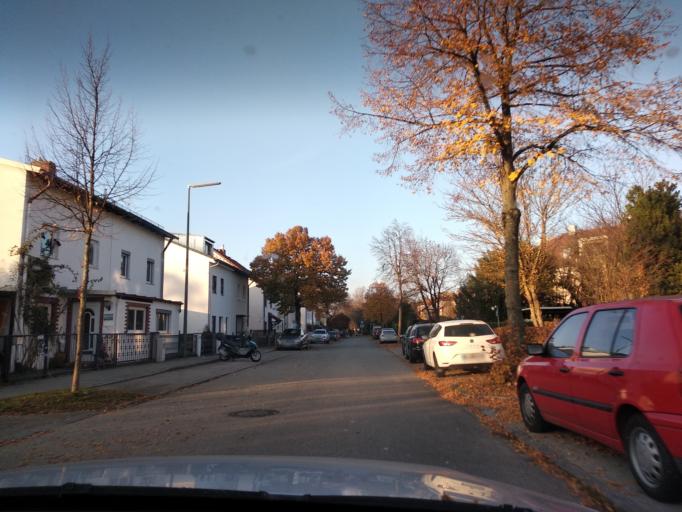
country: DE
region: Bavaria
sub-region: Upper Bavaria
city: Bogenhausen
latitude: 48.1417
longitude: 11.6434
